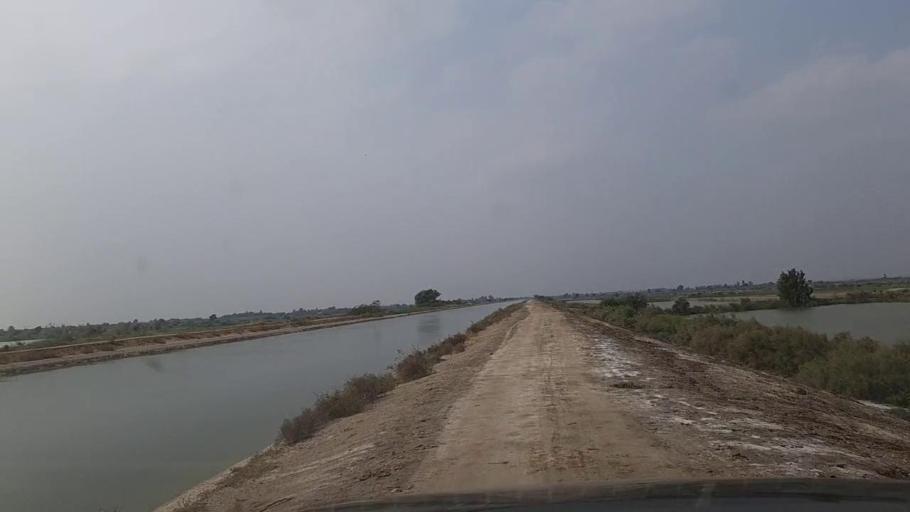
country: PK
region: Sindh
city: Thatta
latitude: 24.8060
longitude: 67.8877
